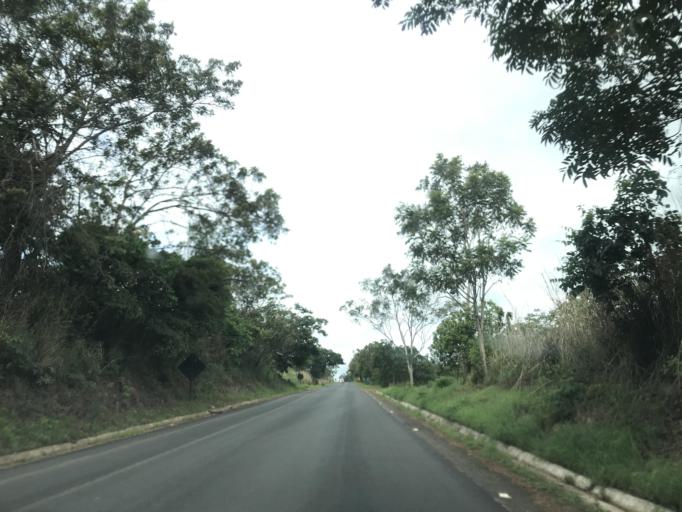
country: BR
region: Goias
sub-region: Bela Vista De Goias
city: Bela Vista de Goias
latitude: -17.0353
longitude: -48.6584
